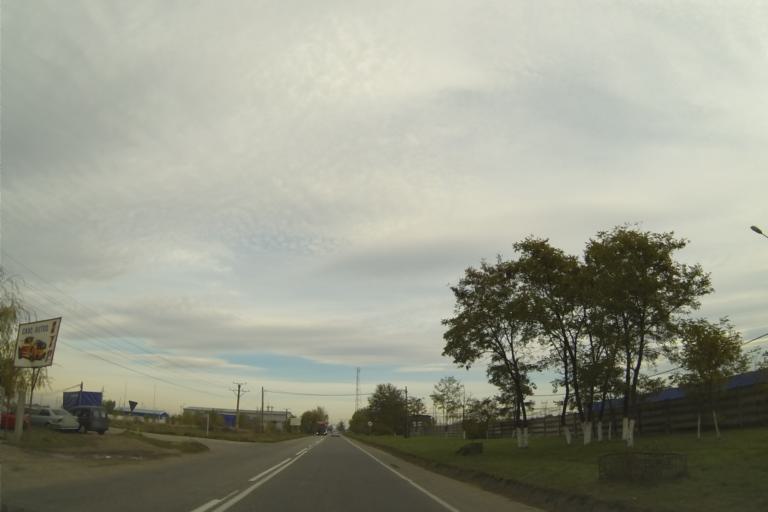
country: RO
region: Olt
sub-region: Municipiul Slatina
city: Slatina
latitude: 44.4497
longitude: 24.3880
